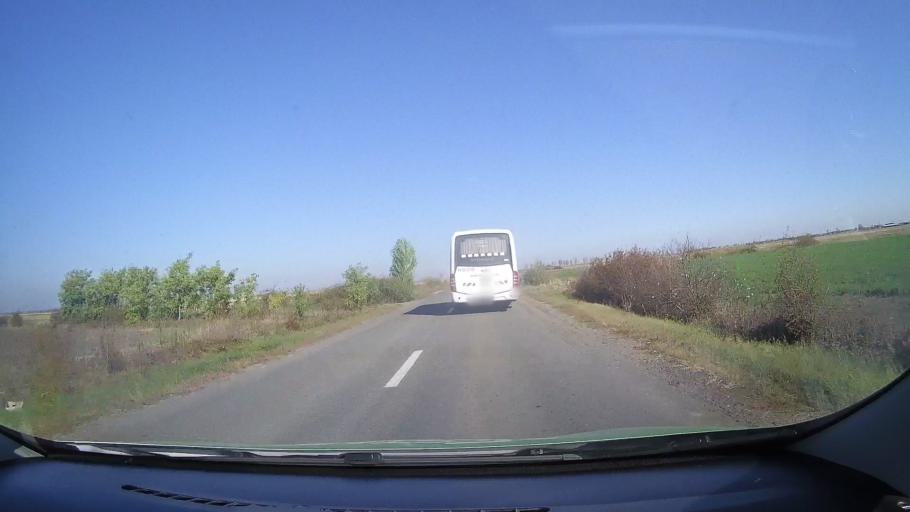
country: RO
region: Satu Mare
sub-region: Comuna Cauas
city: Cauas
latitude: 47.5867
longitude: 22.5472
